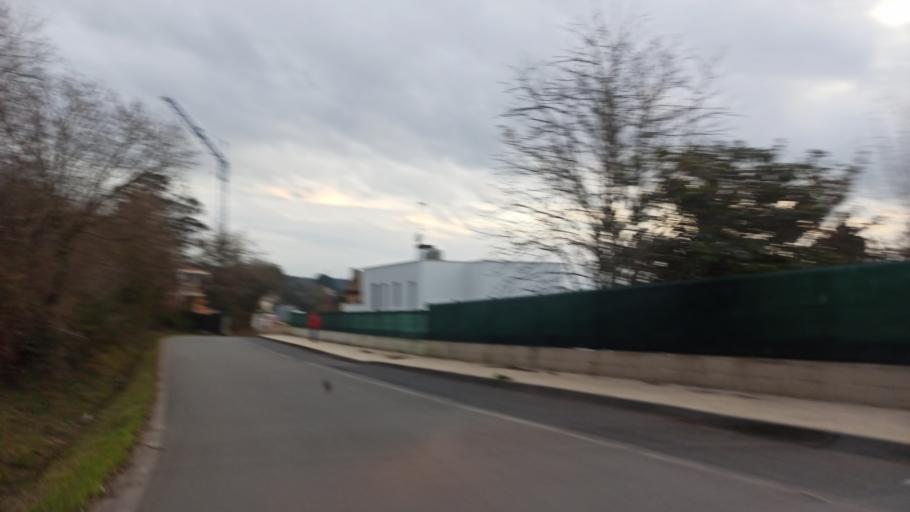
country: ES
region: Galicia
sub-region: Provincia da Coruna
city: Cambre
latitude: 43.3259
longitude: -8.3478
